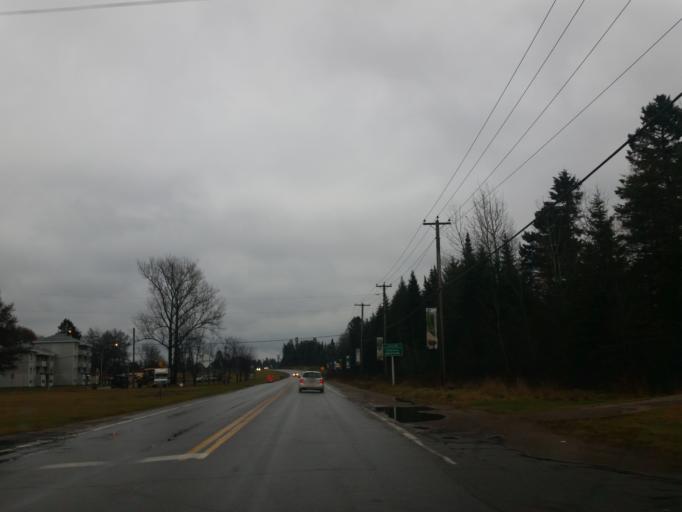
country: CA
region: Quebec
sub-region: Capitale-Nationale
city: Shannon
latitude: 46.8870
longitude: -71.5092
